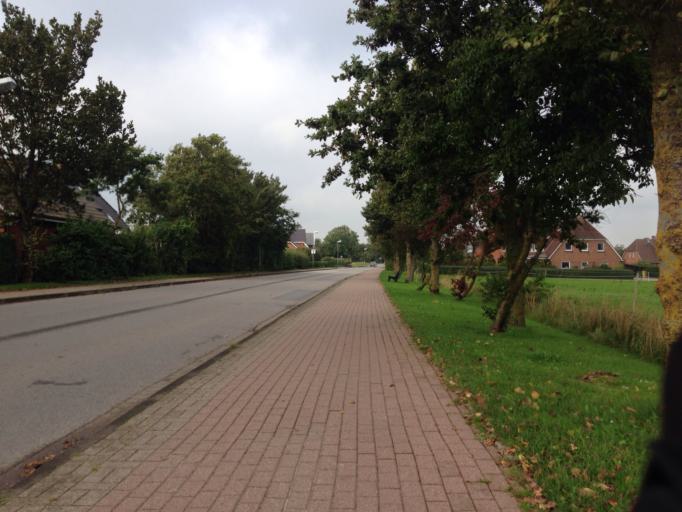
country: DE
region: Schleswig-Holstein
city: Wrixum
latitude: 54.6998
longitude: 8.5471
